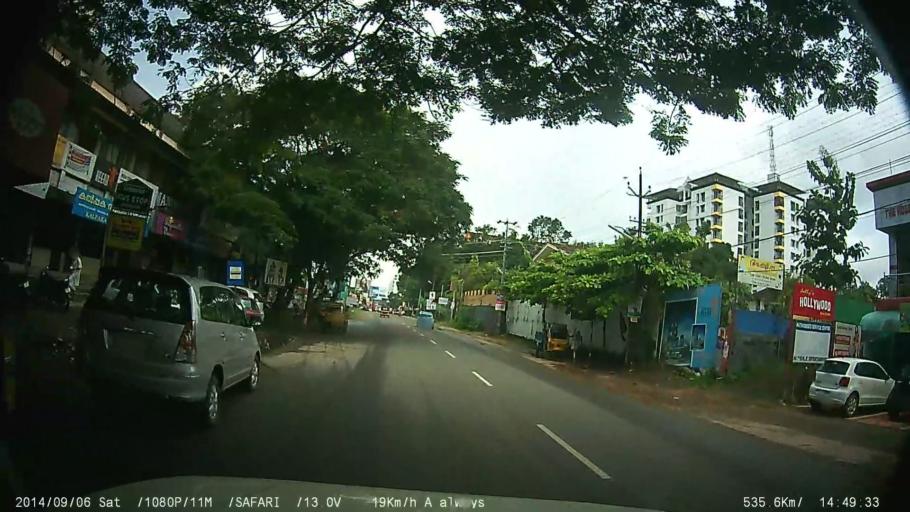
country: IN
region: Kerala
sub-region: Kottayam
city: Kottayam
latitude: 9.5874
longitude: 76.5439
